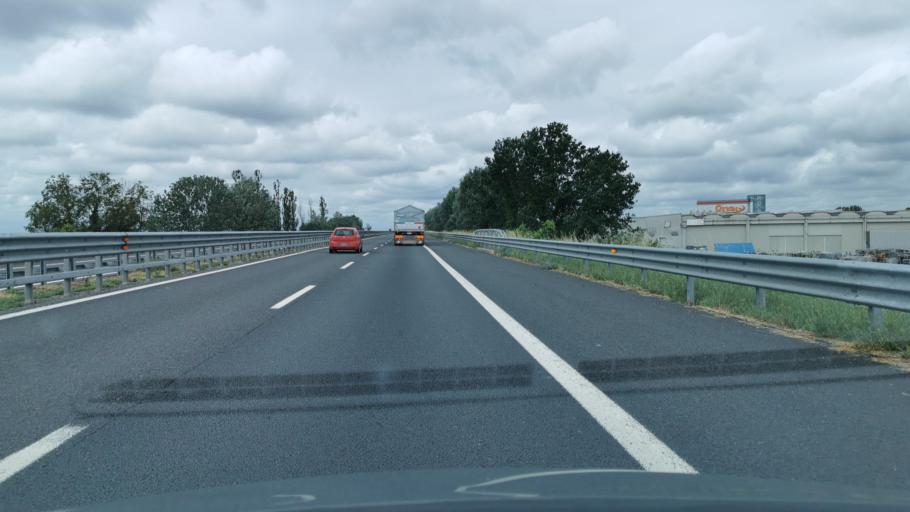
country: IT
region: Emilia-Romagna
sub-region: Provincia di Ravenna
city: Bagnacavallo
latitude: 44.4061
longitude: 11.9948
